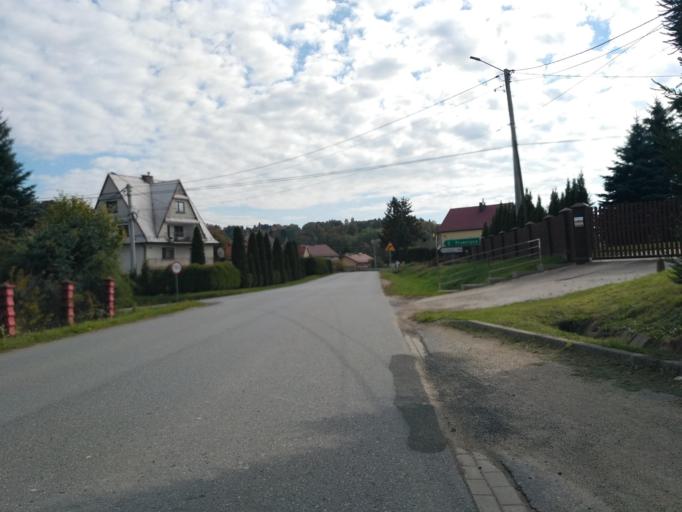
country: PL
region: Subcarpathian Voivodeship
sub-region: Powiat debicki
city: Jodlowa
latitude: 49.8934
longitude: 21.3292
